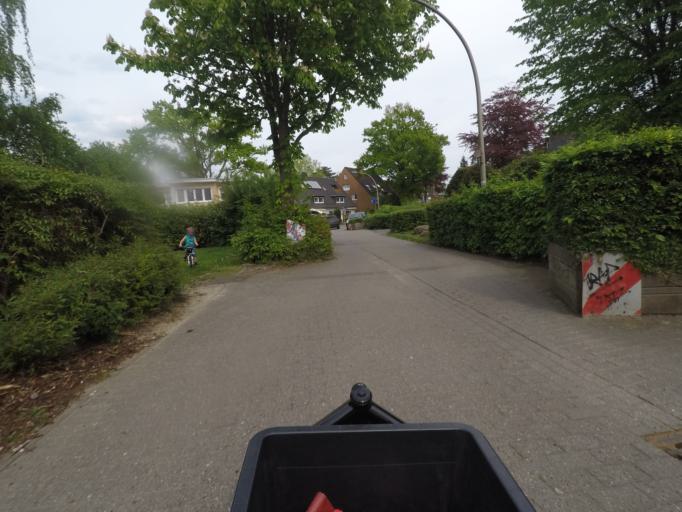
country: DE
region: Hamburg
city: Wellingsbuettel
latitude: 53.6284
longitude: 10.0925
